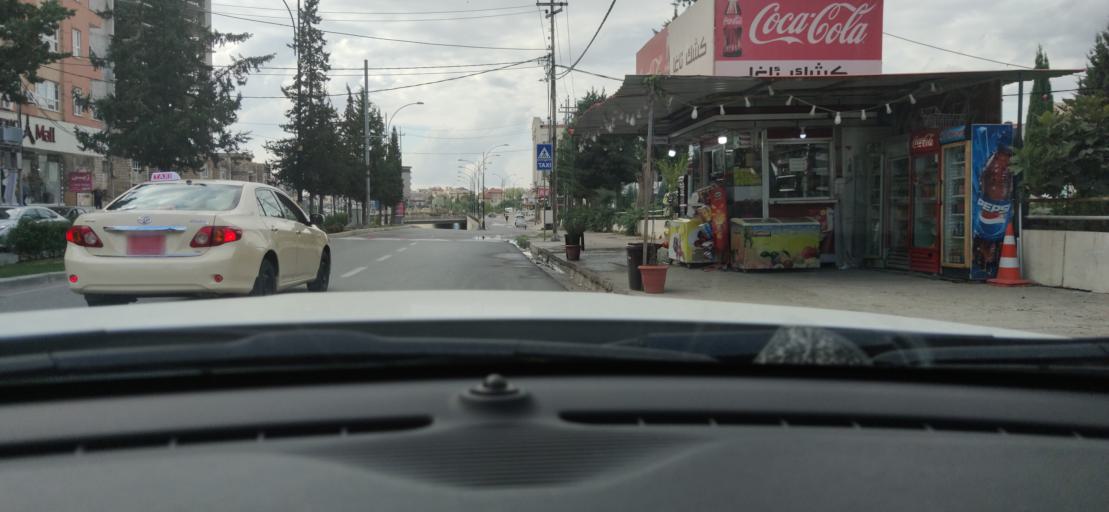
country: IQ
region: Dahuk
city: Dihok
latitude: 36.8669
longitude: 42.9811
